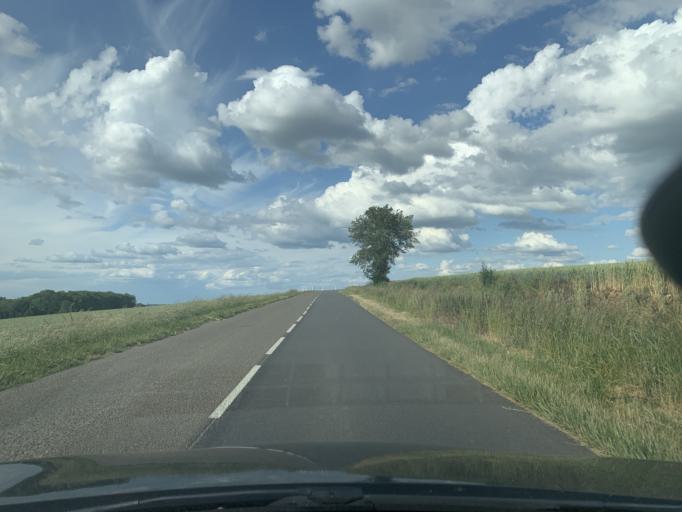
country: FR
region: Nord-Pas-de-Calais
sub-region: Departement du Nord
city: Marcoing
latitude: 50.0967
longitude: 3.1543
